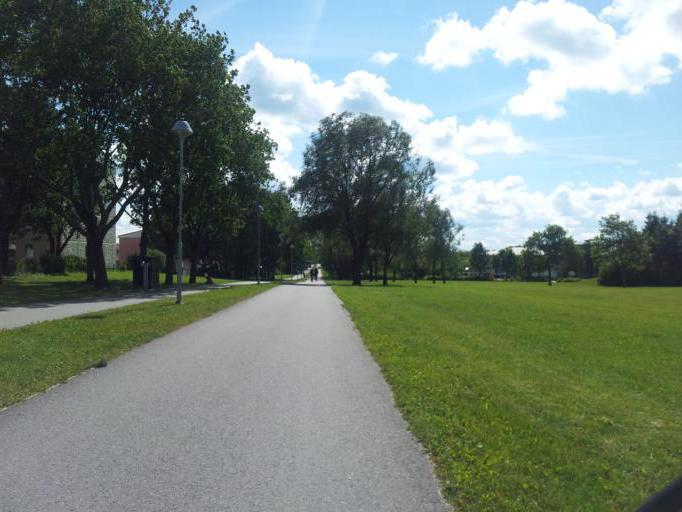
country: SE
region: Uppsala
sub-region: Uppsala Kommun
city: Uppsala
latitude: 59.8745
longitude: 17.6646
